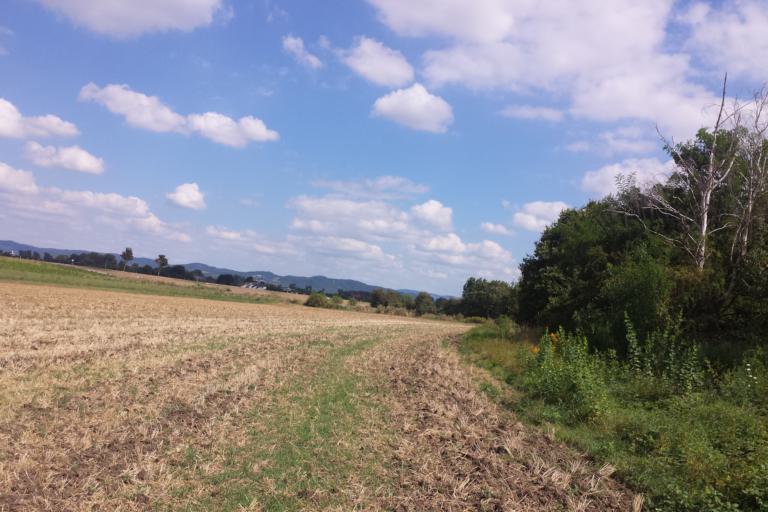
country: DE
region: Hesse
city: Viernheim
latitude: 49.5215
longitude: 8.5842
